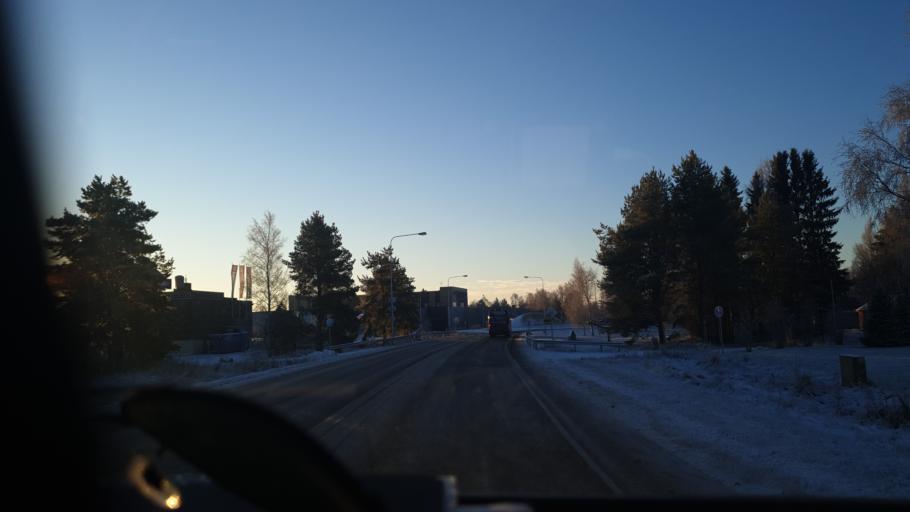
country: FI
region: Northern Ostrobothnia
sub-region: Ylivieska
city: Kalajoki
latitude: 64.2623
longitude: 23.9486
